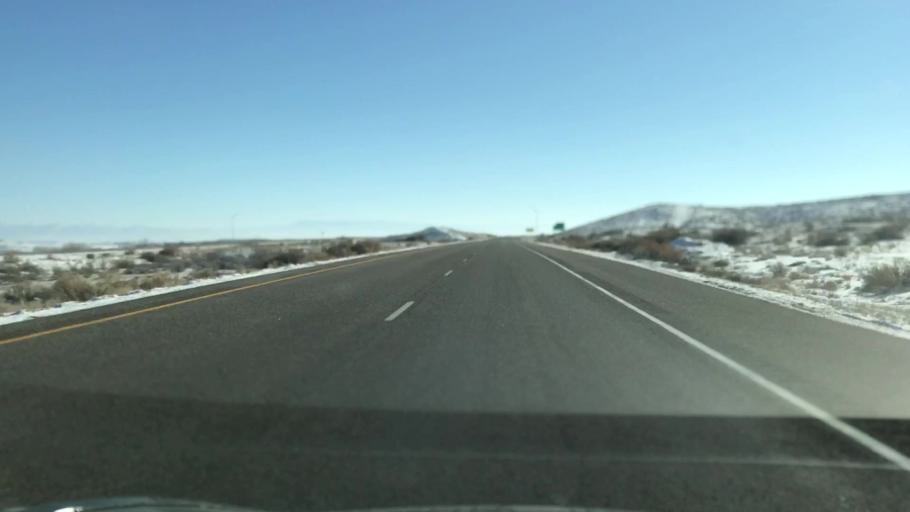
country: US
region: Colorado
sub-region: Mesa County
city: Loma
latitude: 39.2170
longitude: -108.8757
